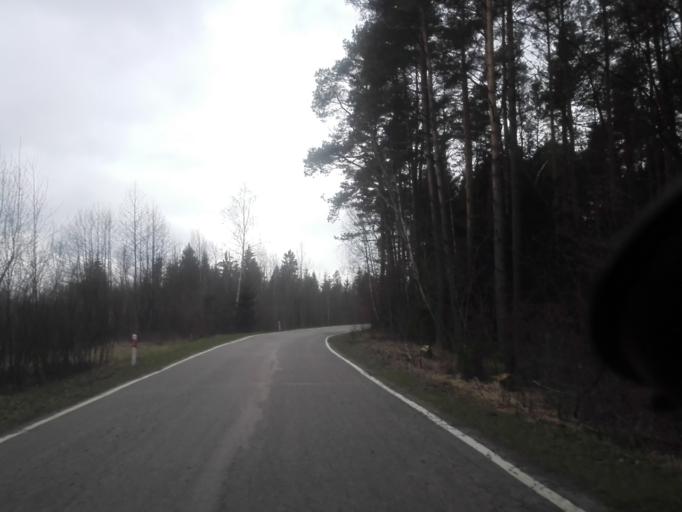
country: PL
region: Podlasie
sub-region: Powiat sejnenski
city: Krasnopol
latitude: 54.1643
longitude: 23.2271
